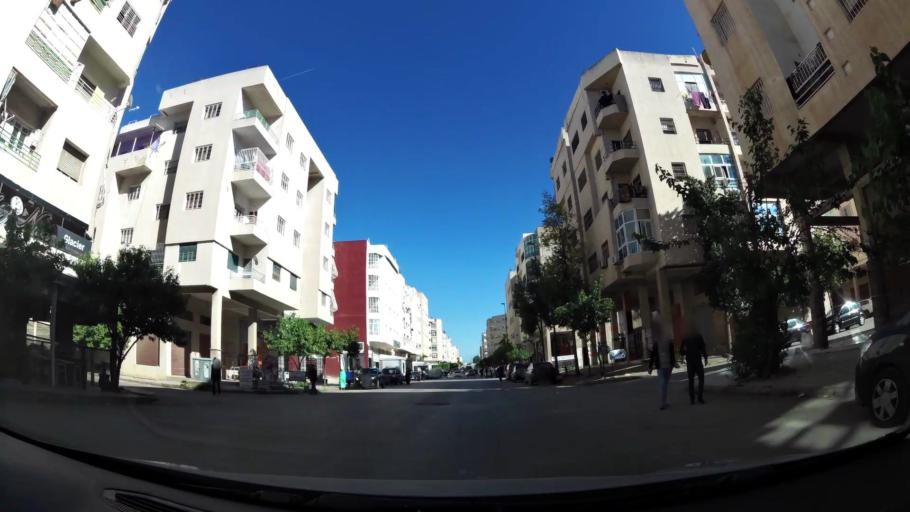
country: MA
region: Fes-Boulemane
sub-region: Fes
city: Fes
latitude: 34.0120
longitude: -4.9672
